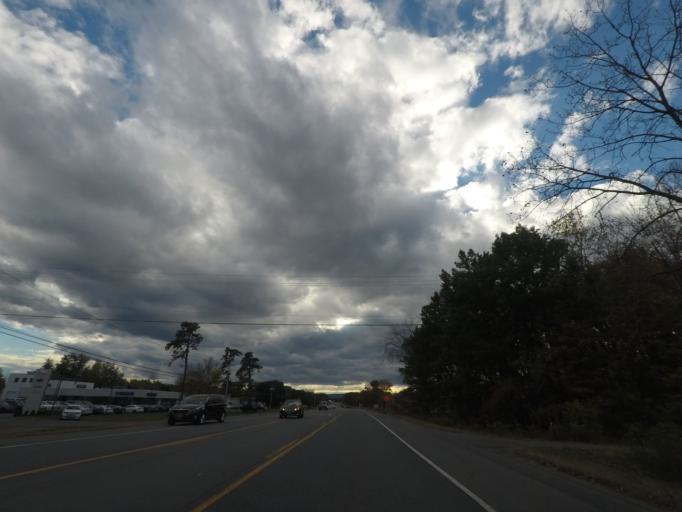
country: US
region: New York
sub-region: Albany County
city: Colonie
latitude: 42.7310
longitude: -73.8526
